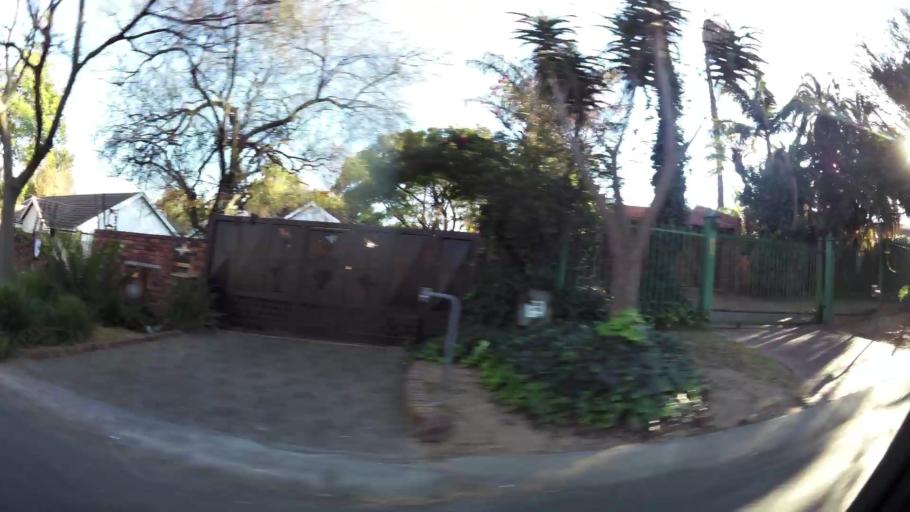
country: ZA
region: Gauteng
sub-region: City of Johannesburg Metropolitan Municipality
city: Midrand
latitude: -26.0352
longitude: 28.0769
